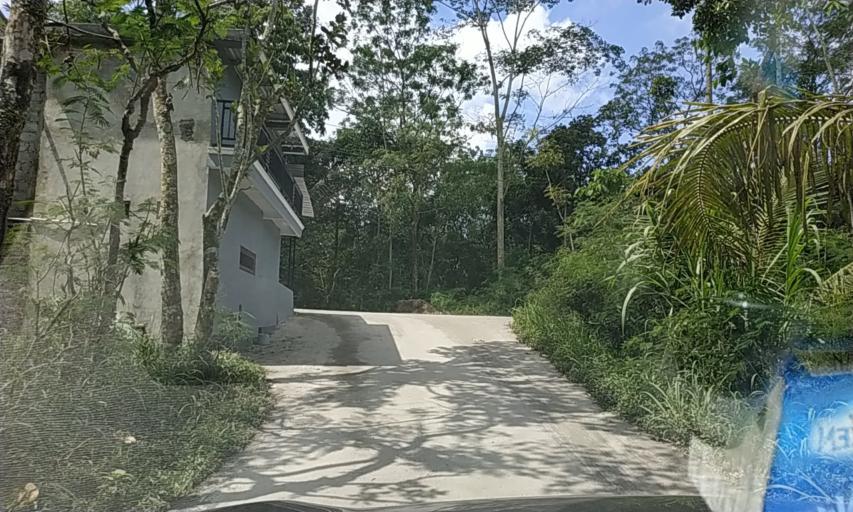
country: ID
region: Central Java
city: Jogonalan
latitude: -7.6284
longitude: 110.4813
